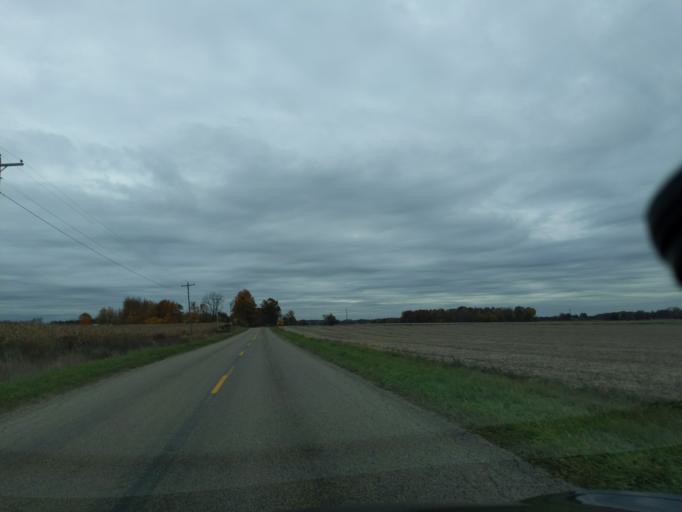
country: US
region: Michigan
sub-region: Eaton County
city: Eaton Rapids
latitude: 42.4395
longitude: -84.6005
